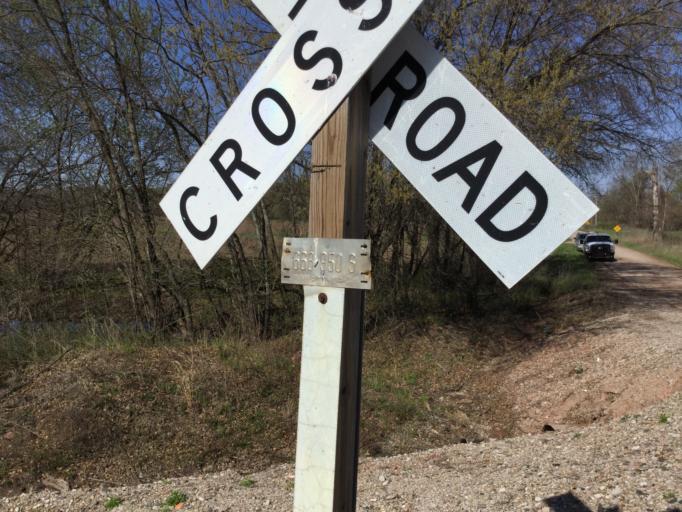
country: US
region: Kansas
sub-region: Crawford County
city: Arma
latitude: 37.6734
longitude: -94.6299
